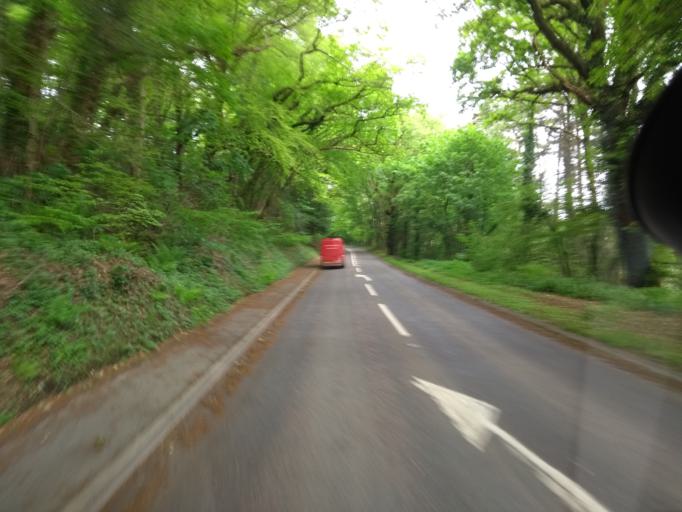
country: GB
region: England
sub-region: Dorset
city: Lyme Regis
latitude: 50.7434
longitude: -2.9224
